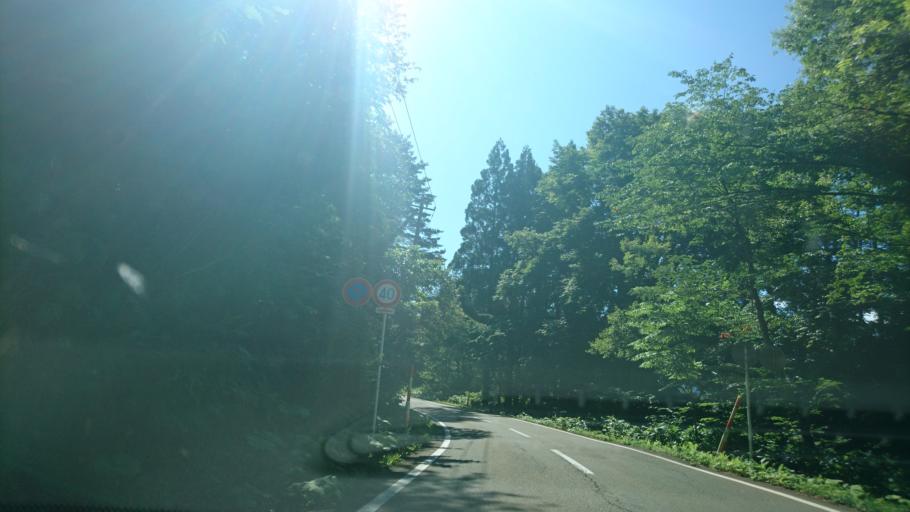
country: JP
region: Akita
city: Kakunodatemachi
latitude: 39.7510
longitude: 140.6564
